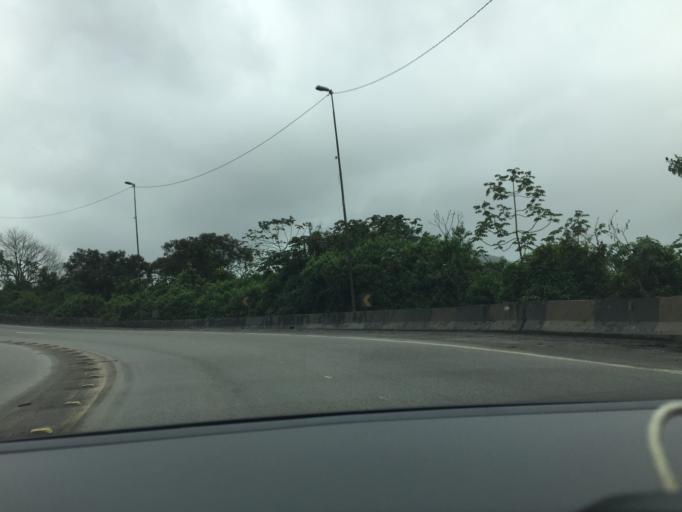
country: BR
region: Sao Paulo
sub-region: Guaruja
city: Guaruja
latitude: -23.9697
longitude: -46.2722
